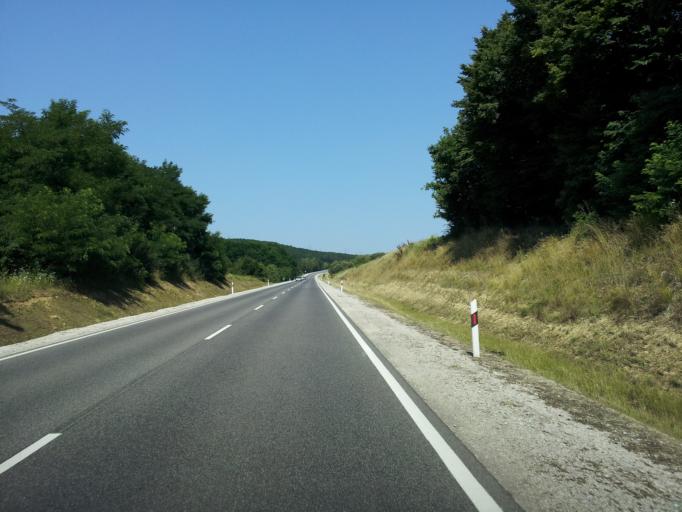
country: HU
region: Zala
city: Pacsa
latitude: 46.8088
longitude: 17.0684
